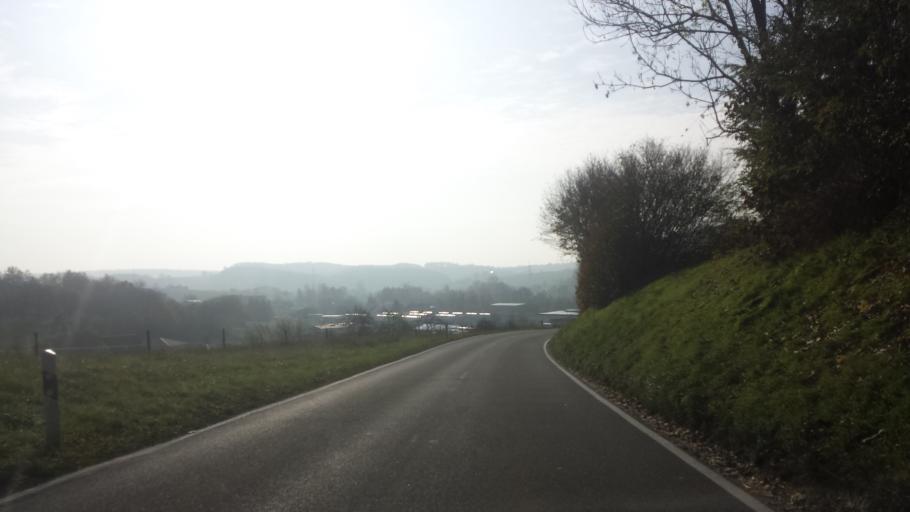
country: DE
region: Baden-Wuerttemberg
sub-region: Karlsruhe Region
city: Neidenstein
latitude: 49.3214
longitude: 8.8963
